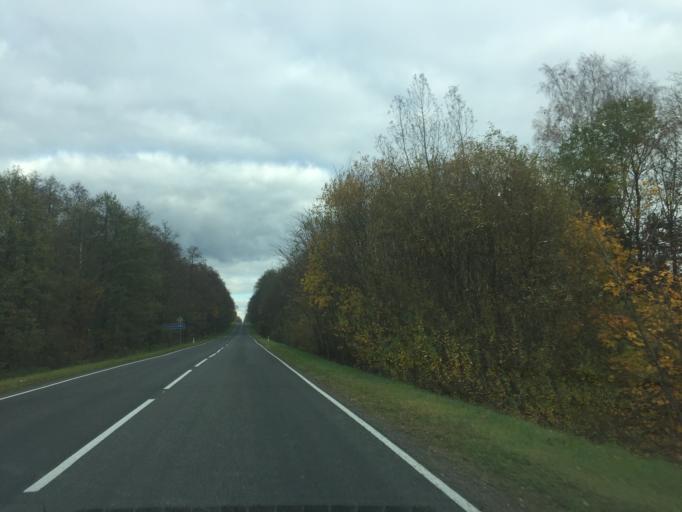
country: BY
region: Minsk
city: Svir
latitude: 54.8973
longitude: 26.4062
